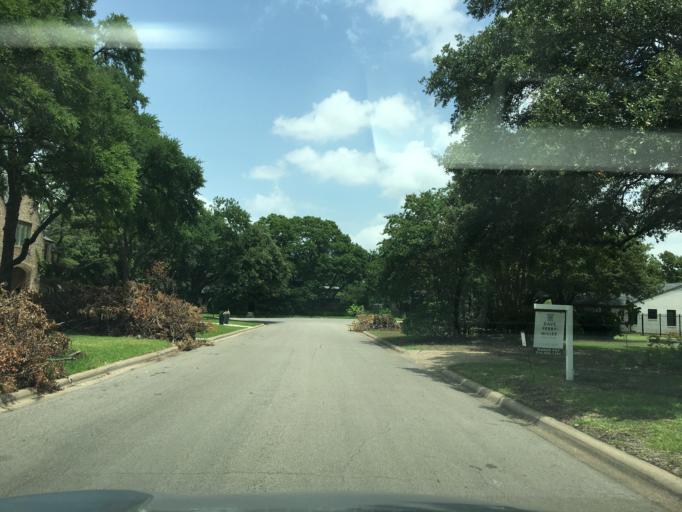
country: US
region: Texas
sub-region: Dallas County
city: University Park
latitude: 32.9046
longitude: -96.7978
